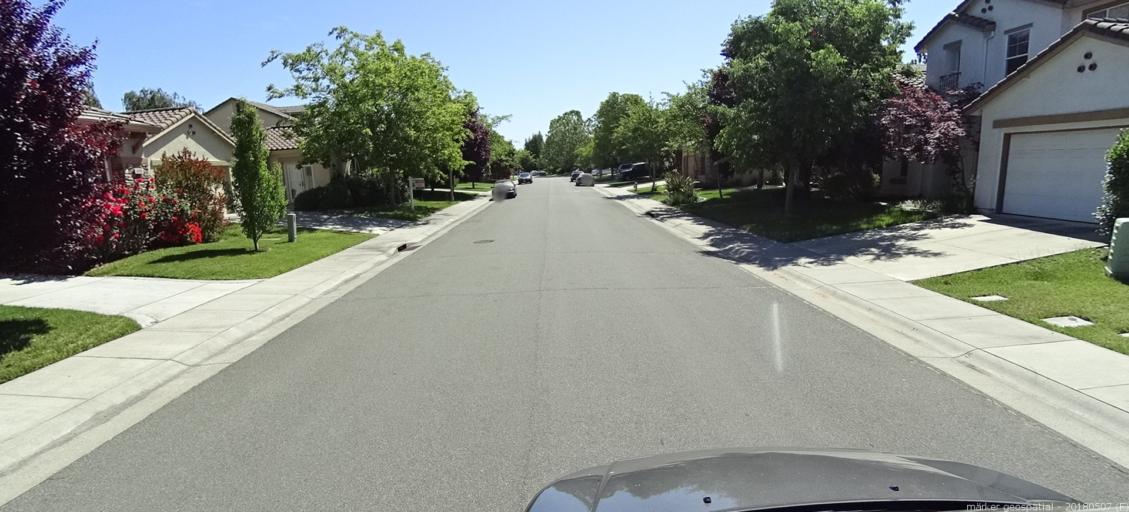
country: US
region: California
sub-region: Sacramento County
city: Rio Linda
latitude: 38.6582
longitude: -121.4986
